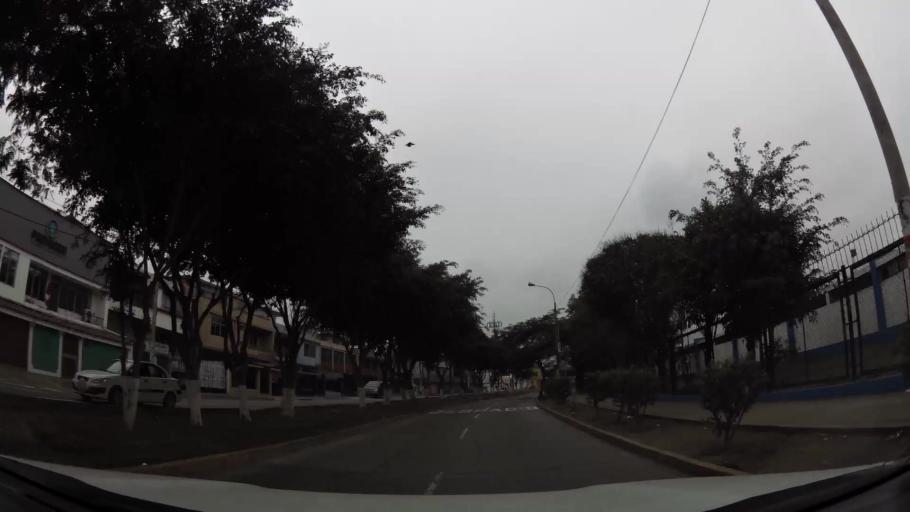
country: PE
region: Lima
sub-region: Lima
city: San Luis
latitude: -12.0843
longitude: -77.0204
